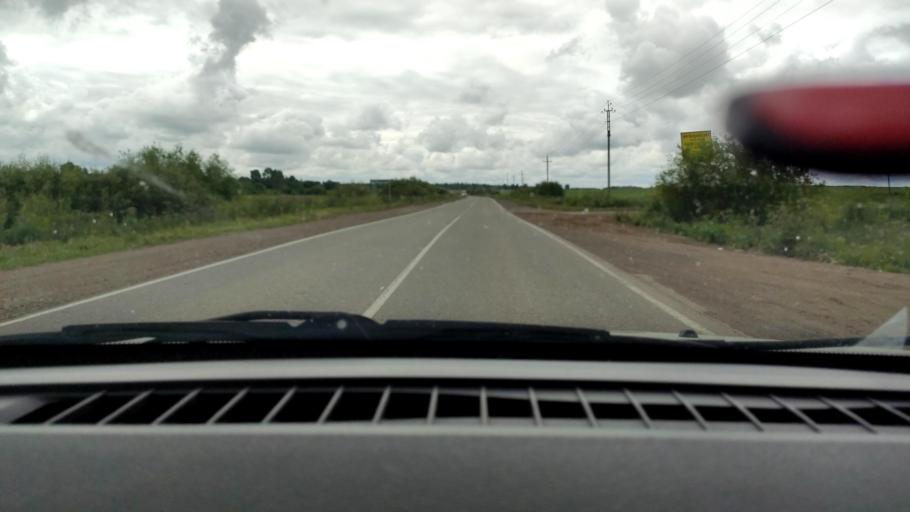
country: RU
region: Perm
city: Ust'-Kachka
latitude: 58.0798
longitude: 55.6172
